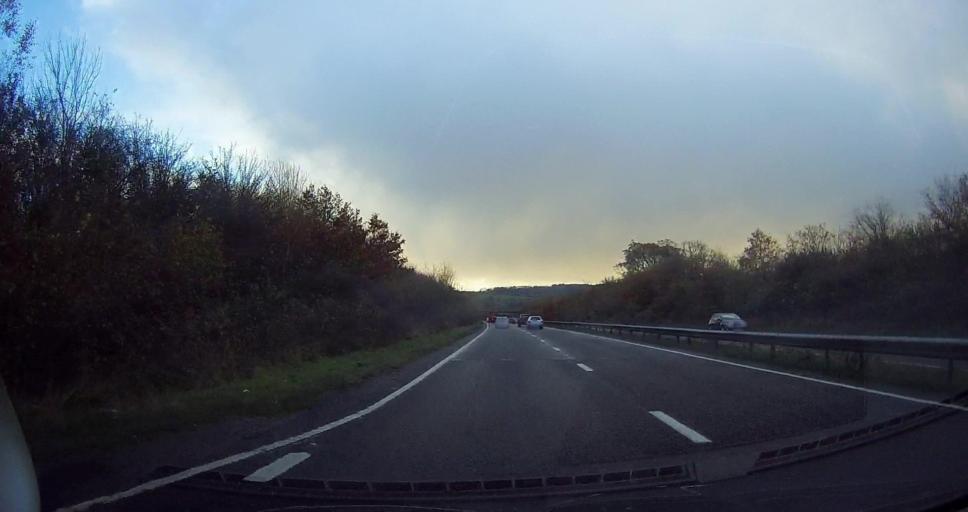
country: GB
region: England
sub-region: West Sussex
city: Hurstpierpoint
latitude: 50.9234
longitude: -0.1939
